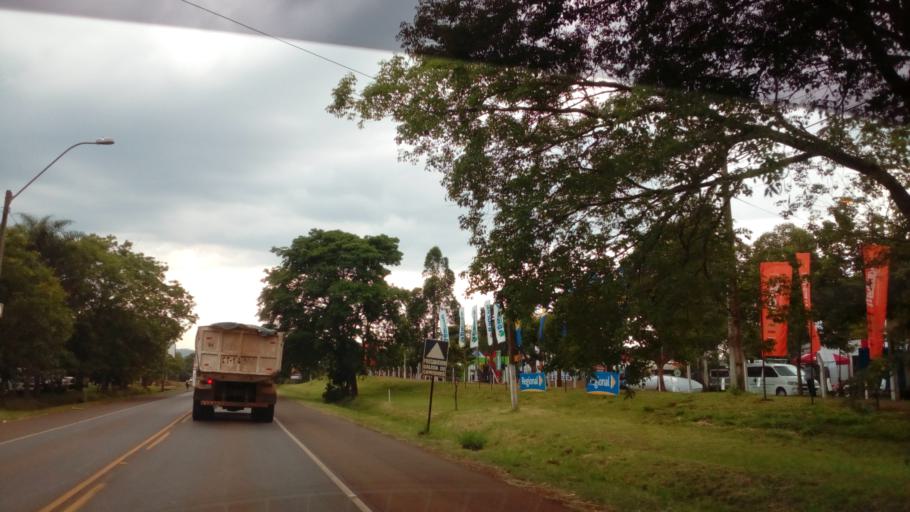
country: PY
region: Itapua
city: Obligado
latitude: -27.0723
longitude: -55.6316
